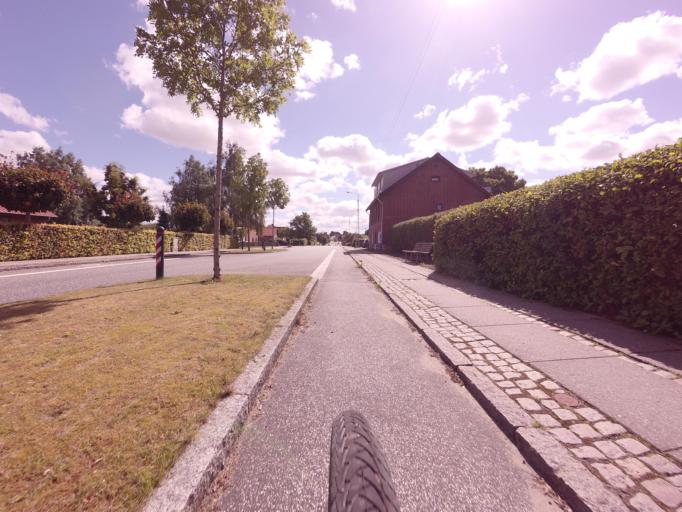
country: DK
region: Central Jutland
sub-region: Horsens Kommune
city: Horsens
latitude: 55.8972
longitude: 9.7599
